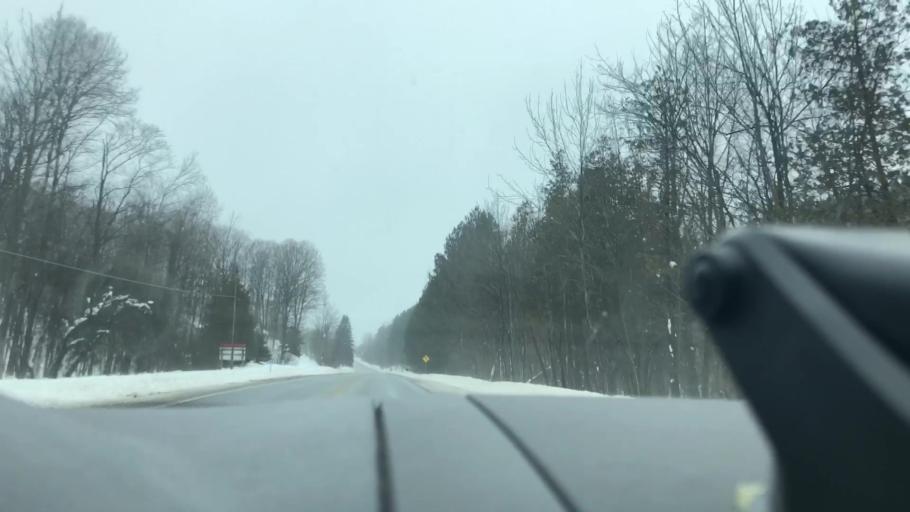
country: US
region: Michigan
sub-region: Charlevoix County
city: East Jordan
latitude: 45.1560
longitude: -85.1537
